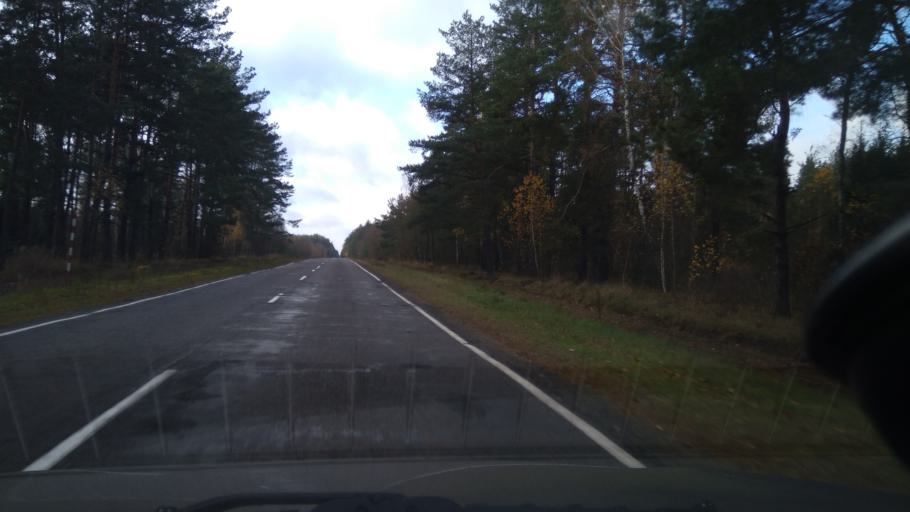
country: BY
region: Minsk
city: Slutsk
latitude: 53.2290
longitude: 27.7173
